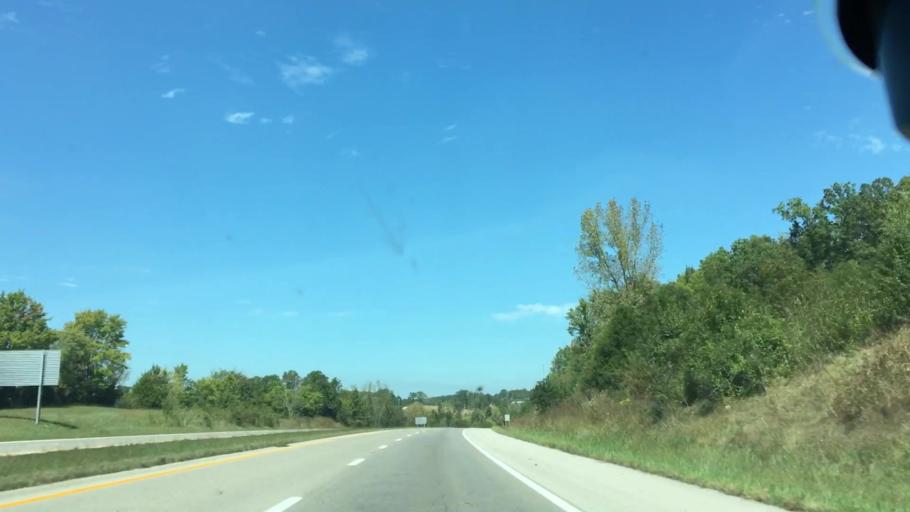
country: US
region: Kentucky
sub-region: Christian County
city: Hopkinsville
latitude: 36.9075
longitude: -87.4735
